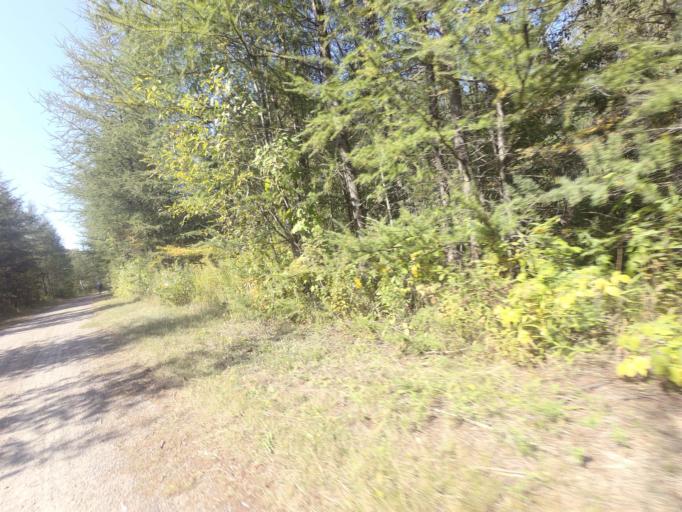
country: CA
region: Quebec
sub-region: Laurentides
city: Sainte-Agathe-des-Monts
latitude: 46.1040
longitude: -74.3923
